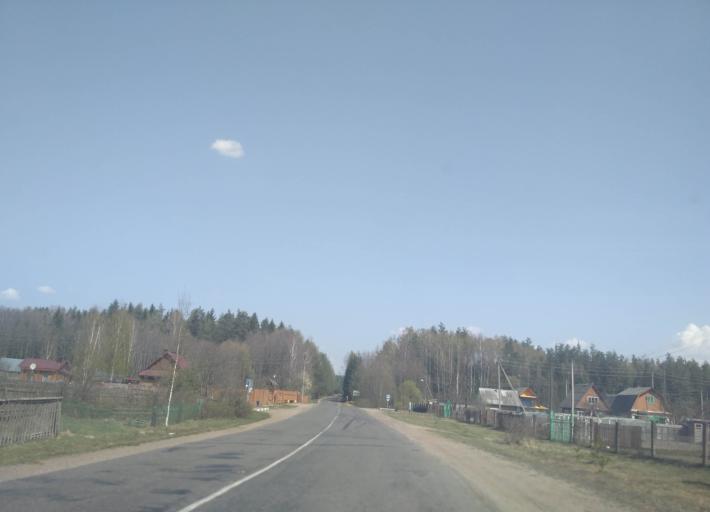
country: BY
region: Minsk
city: Loshnitsa
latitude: 54.4212
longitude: 28.6469
